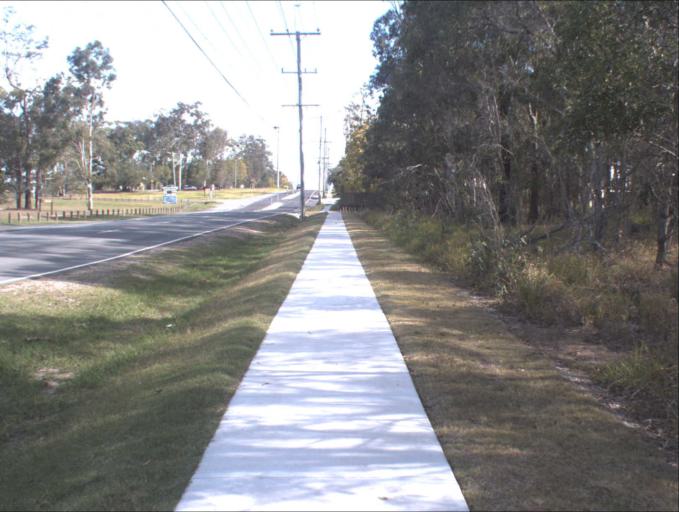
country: AU
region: Queensland
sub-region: Logan
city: Slacks Creek
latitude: -27.6474
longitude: 153.1360
